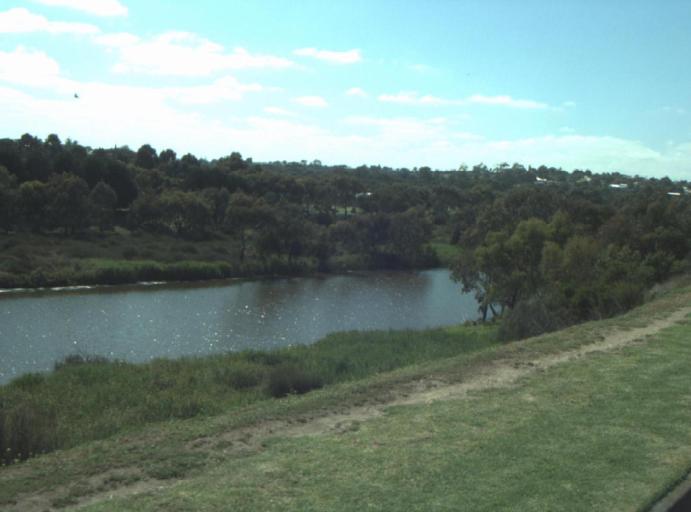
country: AU
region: Victoria
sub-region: Greater Geelong
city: Wandana Heights
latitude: -38.1624
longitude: 144.3226
